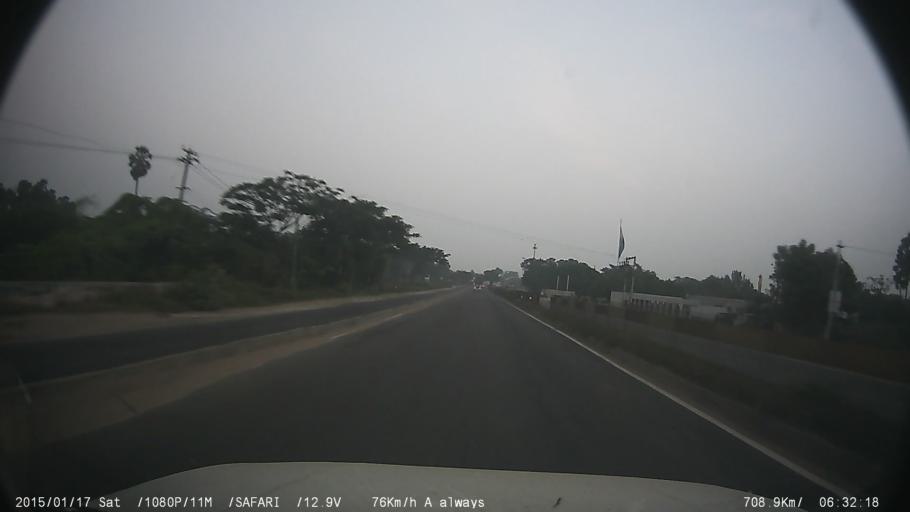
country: IN
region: Tamil Nadu
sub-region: Kancheepuram
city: Sriperumbudur
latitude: 12.9583
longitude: 79.9439
